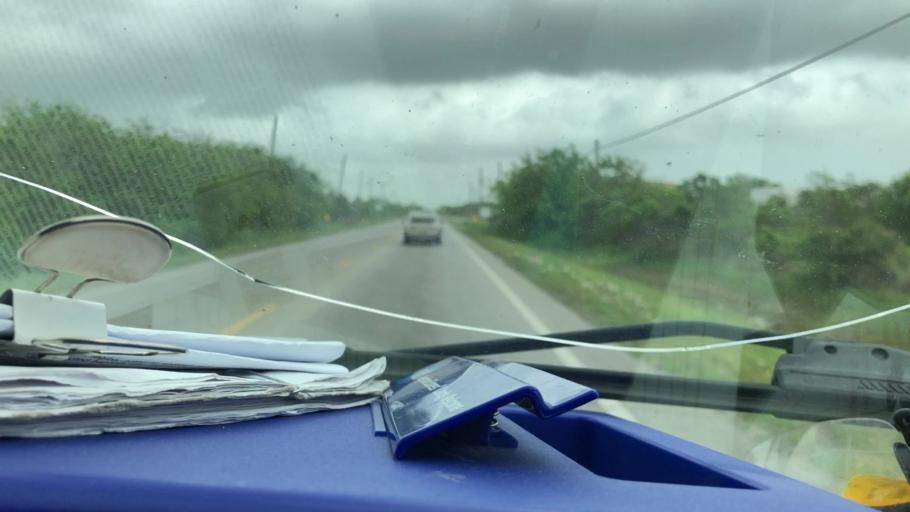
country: US
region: Texas
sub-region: Galveston County
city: Bacliff
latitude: 29.4752
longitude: -94.9716
